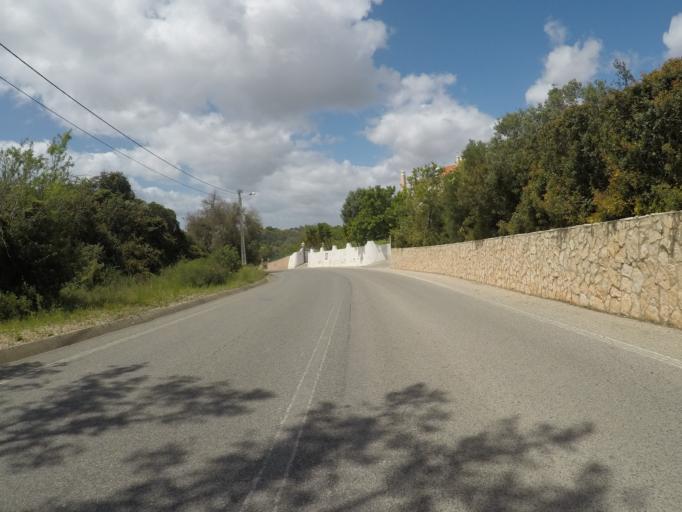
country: PT
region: Faro
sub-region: Lagoa
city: Lagoa
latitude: 37.1163
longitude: -8.4061
